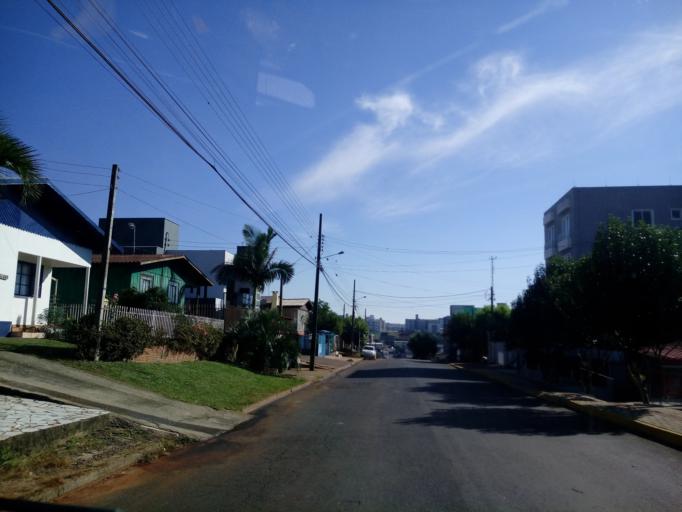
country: BR
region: Santa Catarina
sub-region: Chapeco
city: Chapeco
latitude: -27.1005
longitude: -52.6698
